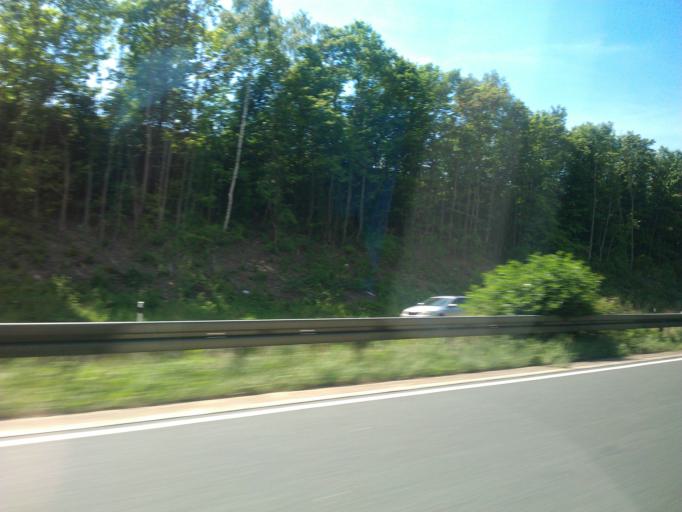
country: DE
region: Rheinland-Pfalz
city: Windhagen
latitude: 50.6710
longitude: 7.3029
